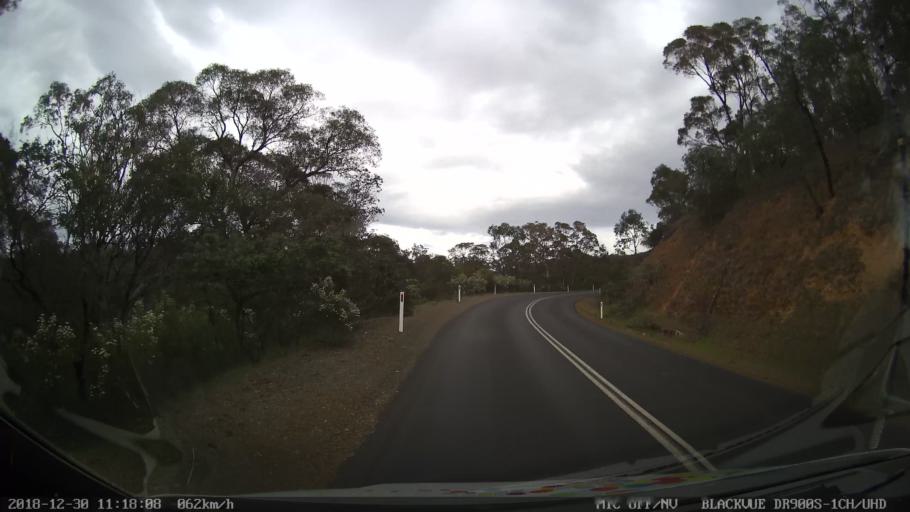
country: AU
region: New South Wales
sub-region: Snowy River
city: Jindabyne
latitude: -36.5338
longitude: 148.6946
